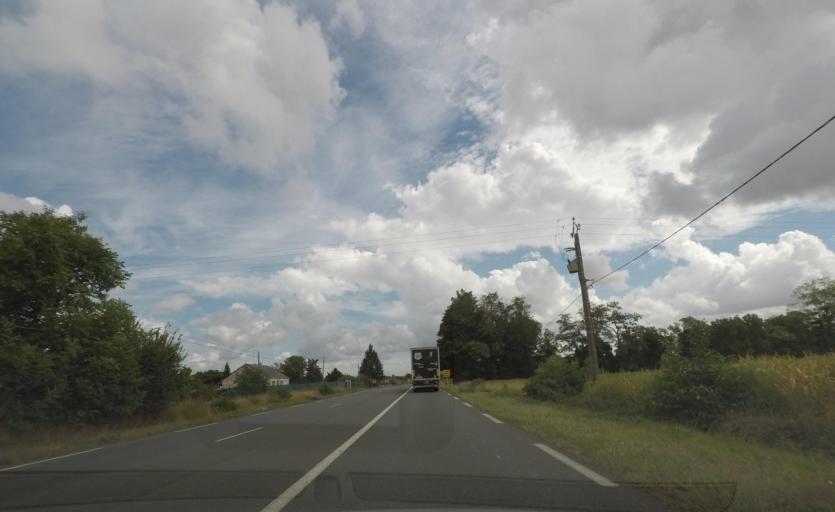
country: FR
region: Pays de la Loire
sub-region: Departement de Maine-et-Loire
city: Seiches-sur-le-Loir
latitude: 47.5638
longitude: -0.3679
